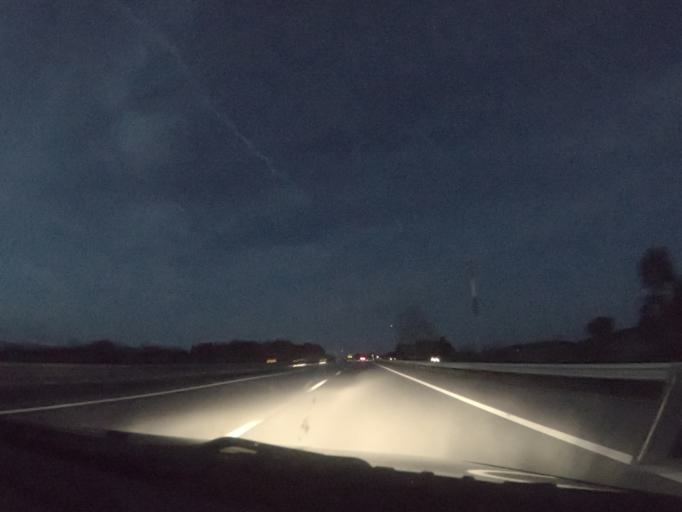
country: PT
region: Guarda
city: Alcains
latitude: 39.9420
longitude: -7.4599
